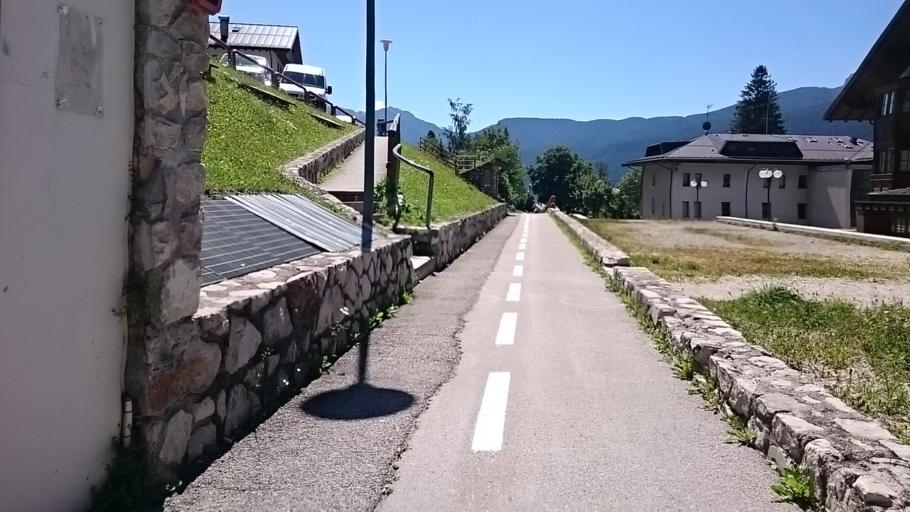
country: IT
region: Veneto
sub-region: Provincia di Belluno
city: San Vito
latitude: 46.4623
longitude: 12.2053
